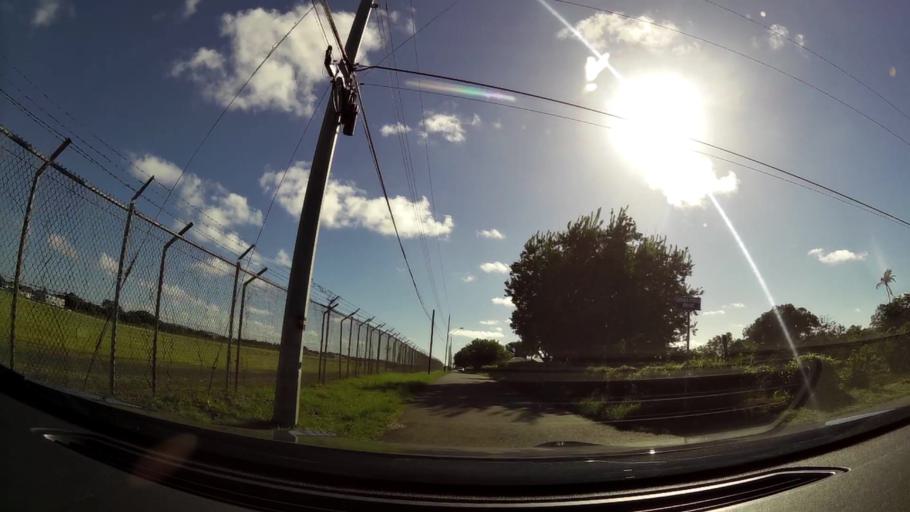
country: TT
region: Tobago
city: Scarborough
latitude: 11.1494
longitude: -60.8408
